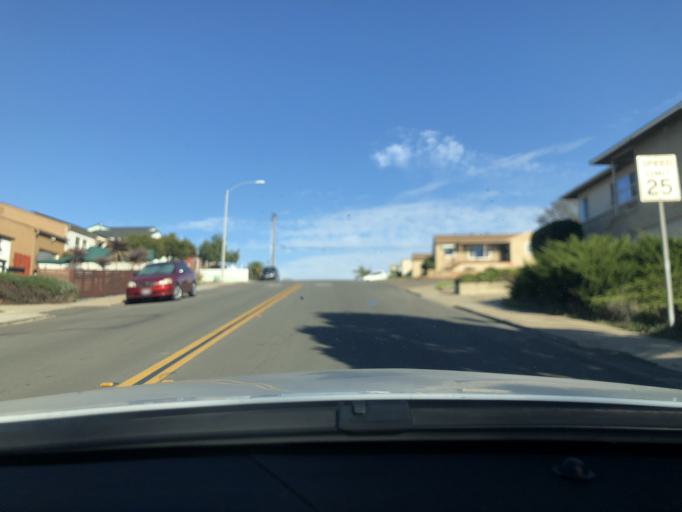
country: US
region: California
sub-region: San Diego County
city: Lemon Grove
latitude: 32.7551
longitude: -117.0723
